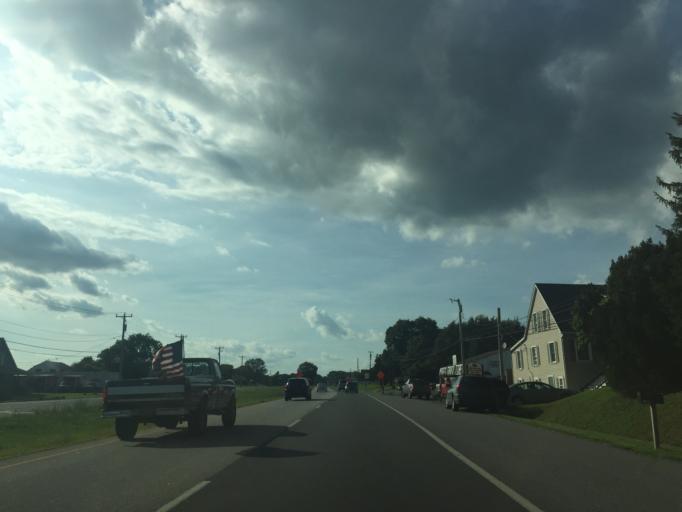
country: US
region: Delaware
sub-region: Kent County
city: Smyrna
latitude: 39.3108
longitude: -75.6109
